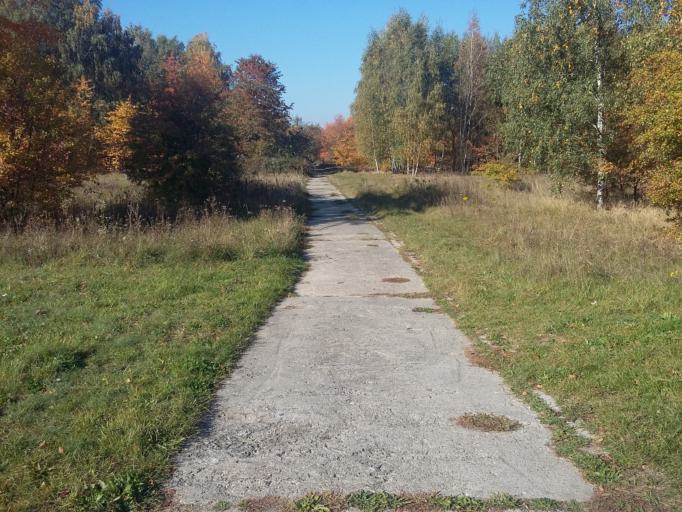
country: PL
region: Lodz Voivodeship
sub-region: Powiat pabianicki
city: Ksawerow
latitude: 51.7289
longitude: 19.4048
